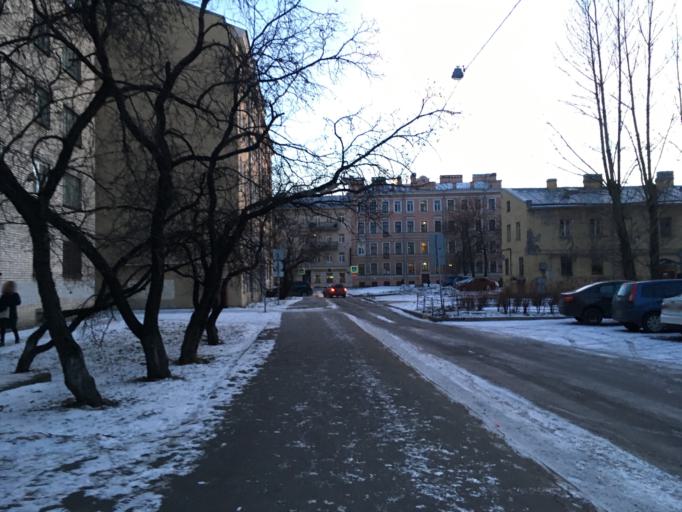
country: RU
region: St.-Petersburg
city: Centralniy
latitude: 59.9091
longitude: 30.3432
